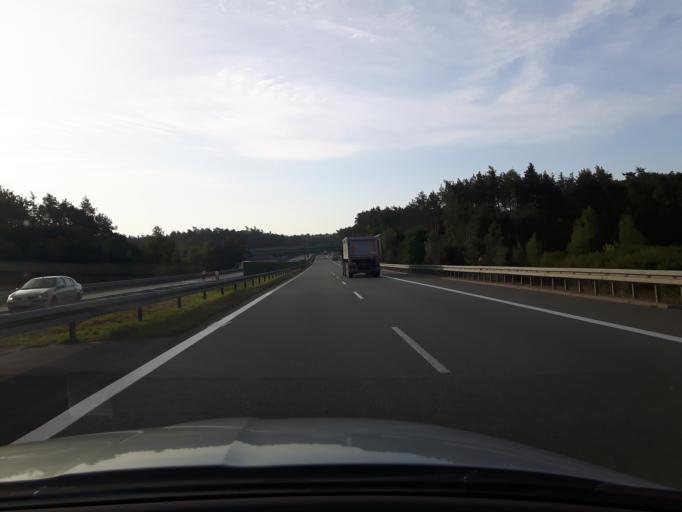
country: PL
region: Masovian Voivodeship
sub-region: Powiat bialobrzeski
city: Bialobrzegi
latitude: 51.6519
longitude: 20.9700
